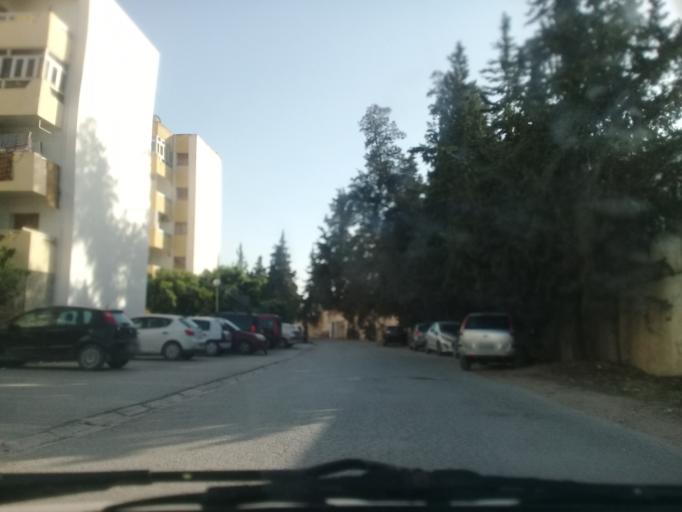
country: TN
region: Ariana
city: Ariana
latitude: 36.8387
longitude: 10.1918
